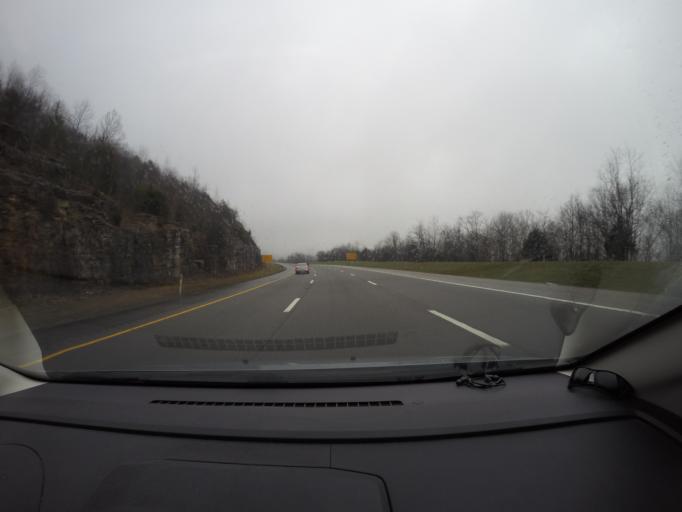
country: US
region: Tennessee
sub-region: Marion County
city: Monteagle
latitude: 35.1908
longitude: -85.8162
